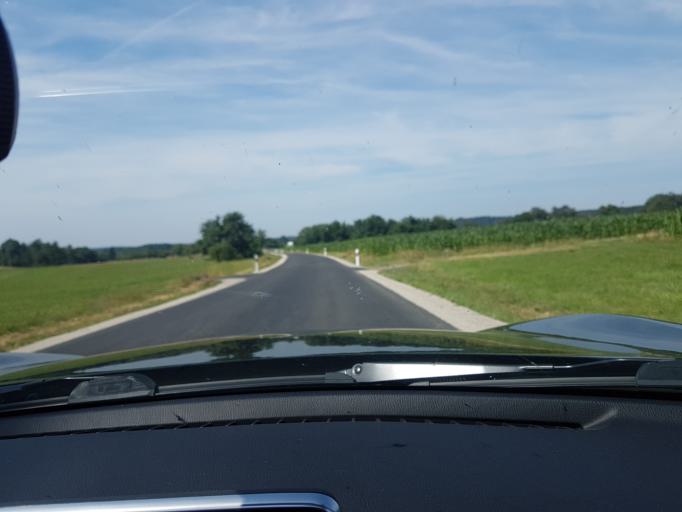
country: DE
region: Baden-Wuerttemberg
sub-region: Karlsruhe Region
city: Limbach
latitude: 49.4448
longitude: 9.1831
